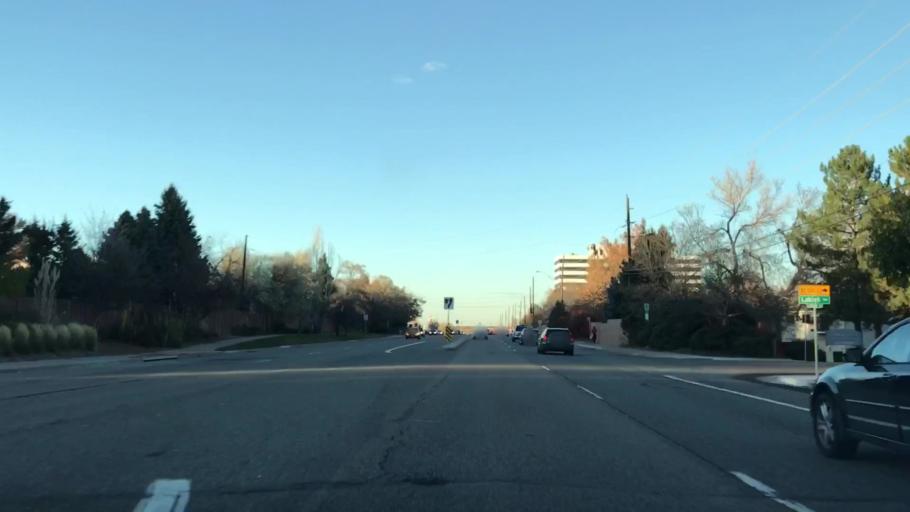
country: US
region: Colorado
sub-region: Arapahoe County
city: Castlewood
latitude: 39.6475
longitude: -104.8849
